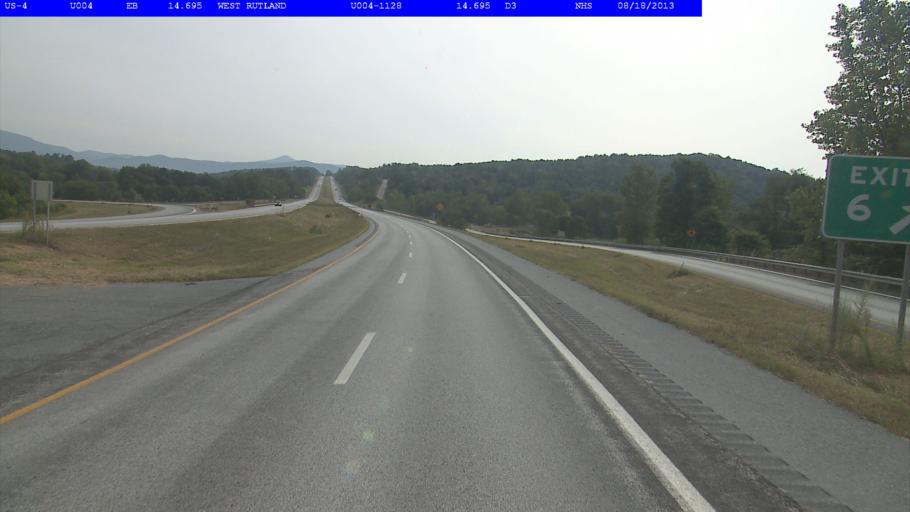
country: US
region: Vermont
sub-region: Rutland County
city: West Rutland
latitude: 43.5877
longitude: -73.0438
